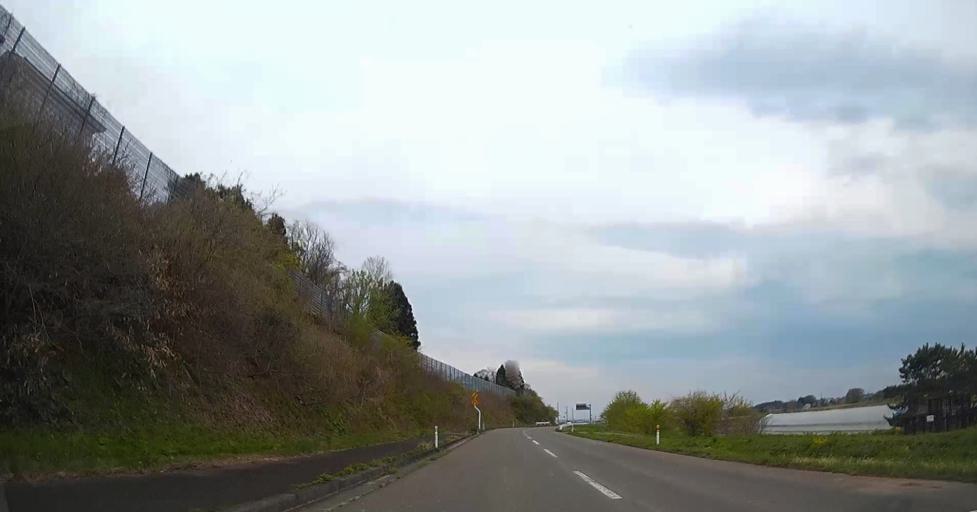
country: JP
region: Aomori
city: Goshogawara
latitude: 40.8985
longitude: 140.4881
